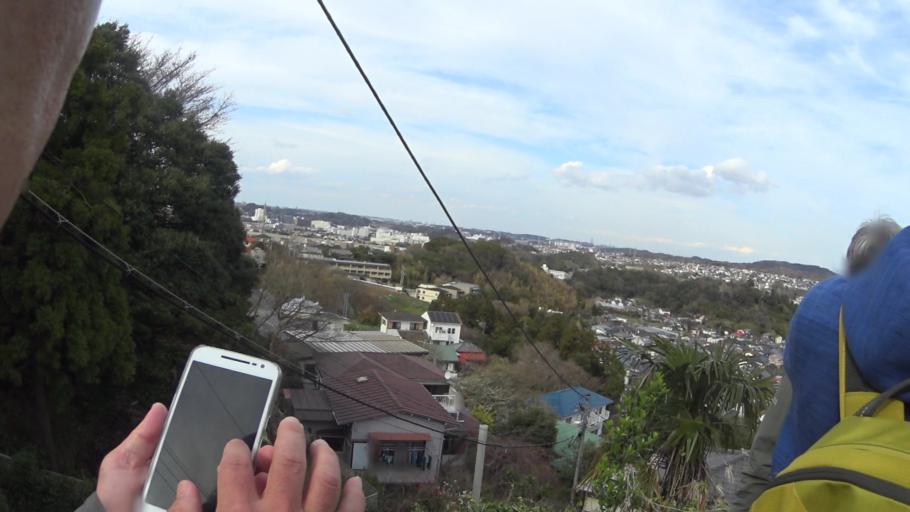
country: JP
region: Kanagawa
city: Kamakura
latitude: 35.3219
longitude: 139.5141
